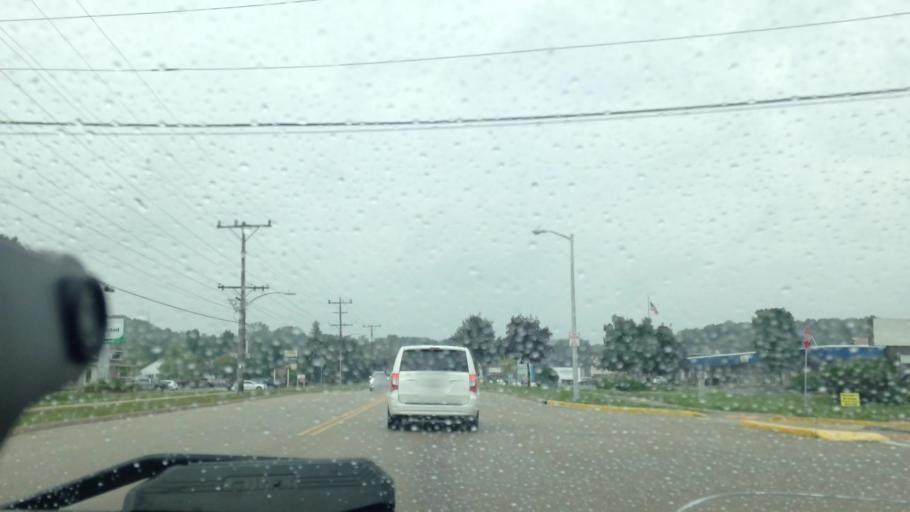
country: US
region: Wisconsin
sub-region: Washington County
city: Slinger
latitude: 43.3313
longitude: -88.2804
